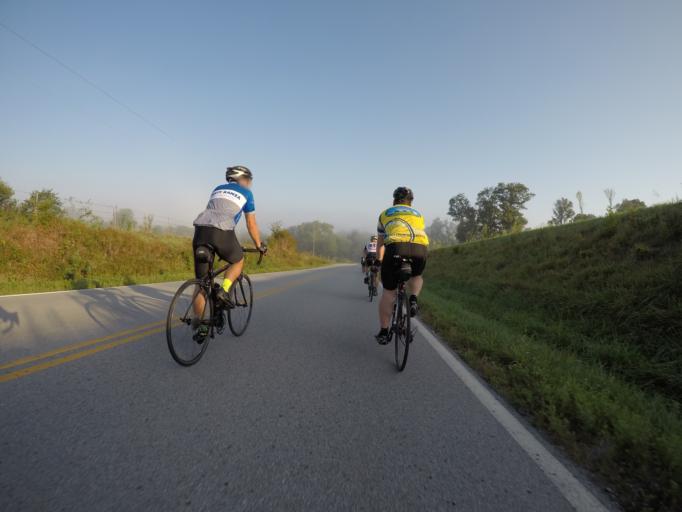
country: US
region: Kansas
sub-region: Leavenworth County
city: Lansing
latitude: 39.2352
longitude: -94.8645
